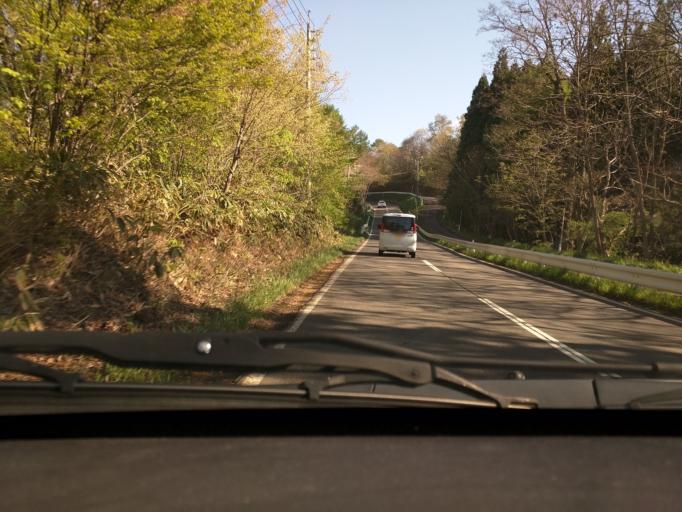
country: JP
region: Nagano
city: Nagano-shi
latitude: 36.6992
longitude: 138.1528
